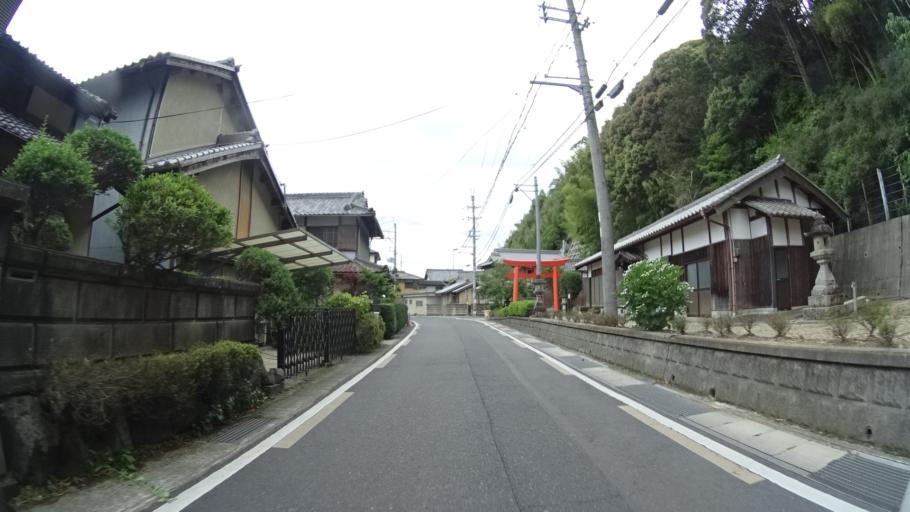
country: JP
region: Nara
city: Nara-shi
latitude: 34.7535
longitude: 135.8561
